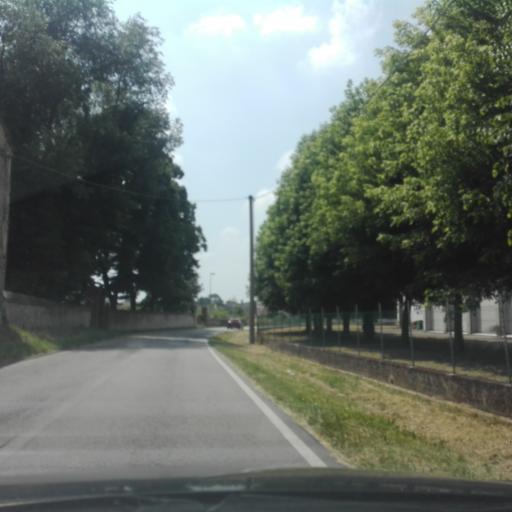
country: IT
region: Veneto
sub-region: Provincia di Rovigo
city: Crespino
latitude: 44.9861
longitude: 11.8925
